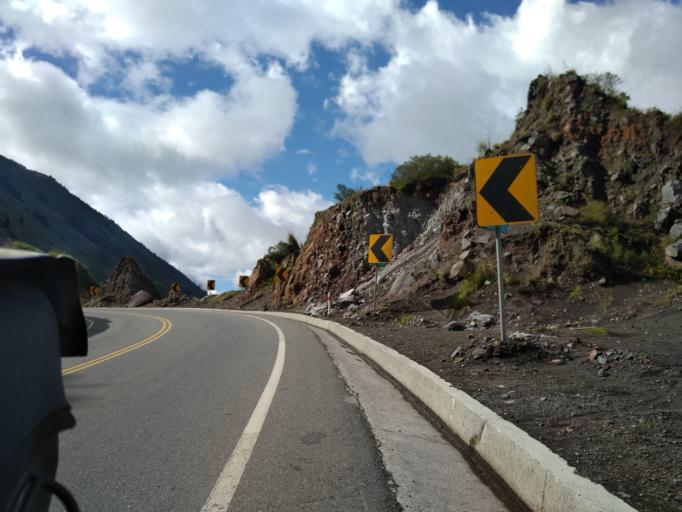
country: EC
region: Tungurahua
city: Banos
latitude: -1.4883
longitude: -78.5170
